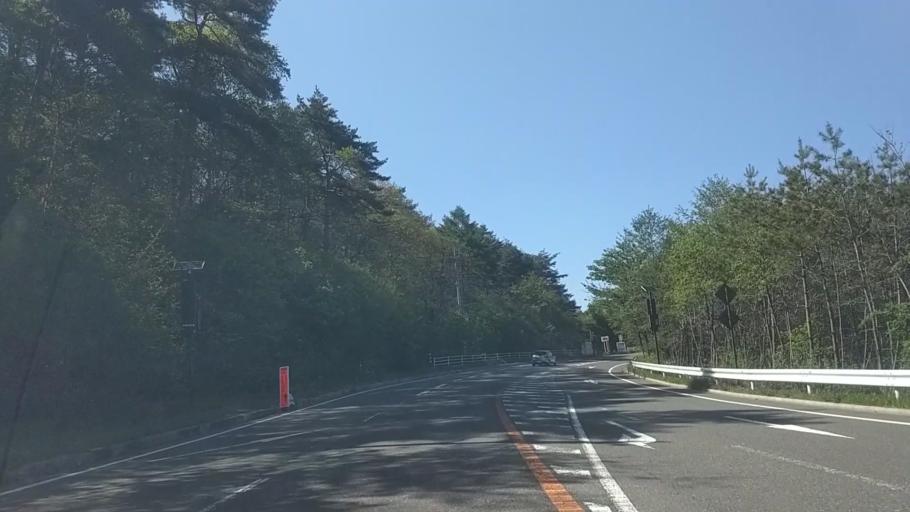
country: JP
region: Yamanashi
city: Nirasaki
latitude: 35.9243
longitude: 138.4397
